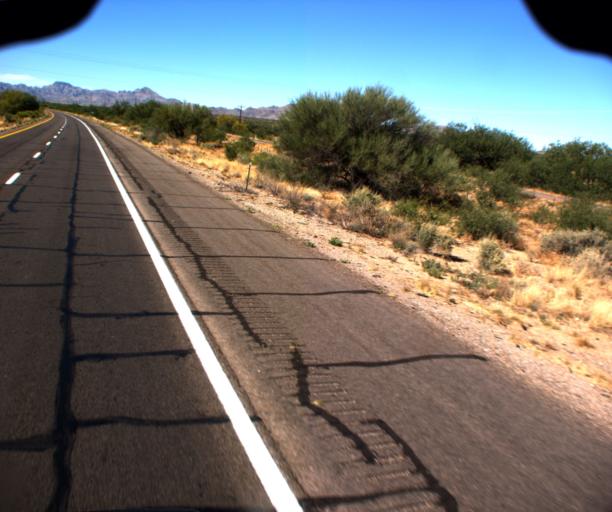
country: US
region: Arizona
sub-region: Pima County
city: Arivaca Junction
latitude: 31.7159
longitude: -111.0633
